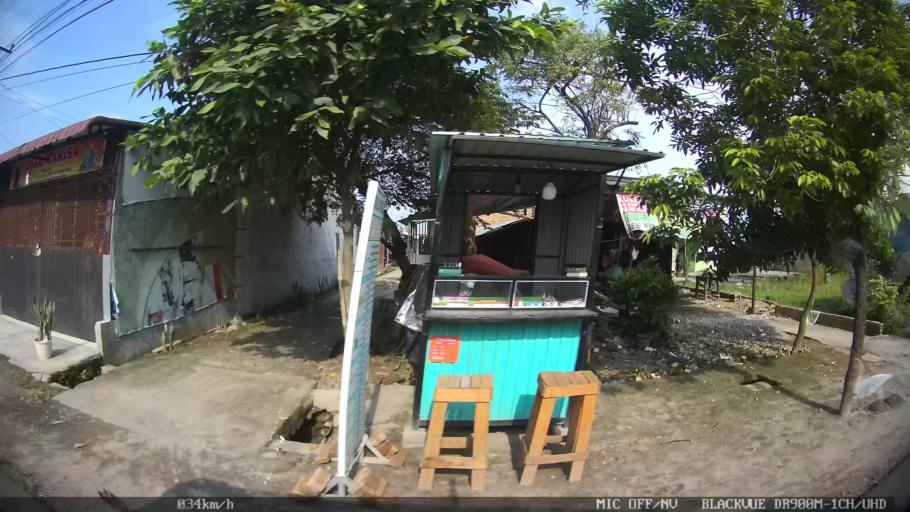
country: ID
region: North Sumatra
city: Medan
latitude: 3.5777
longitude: 98.7567
